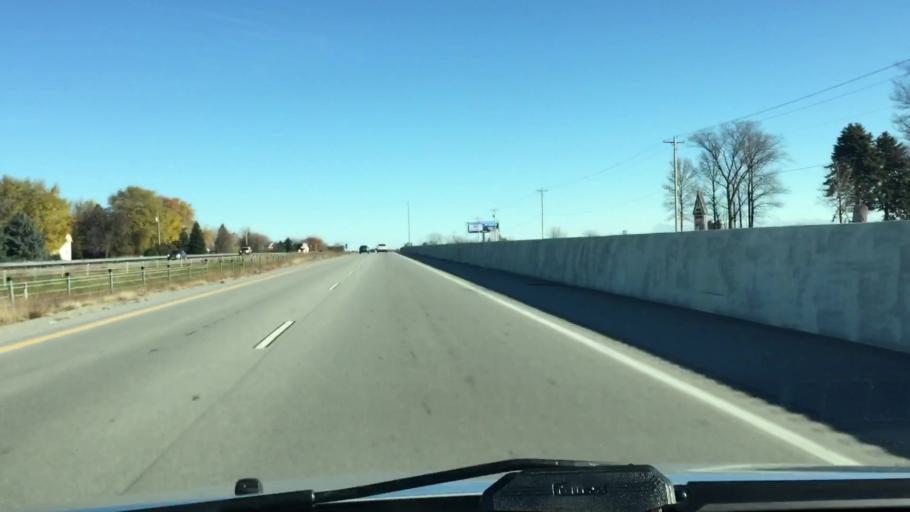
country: US
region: Wisconsin
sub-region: Brown County
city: Wrightstown
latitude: 44.3662
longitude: -88.1781
